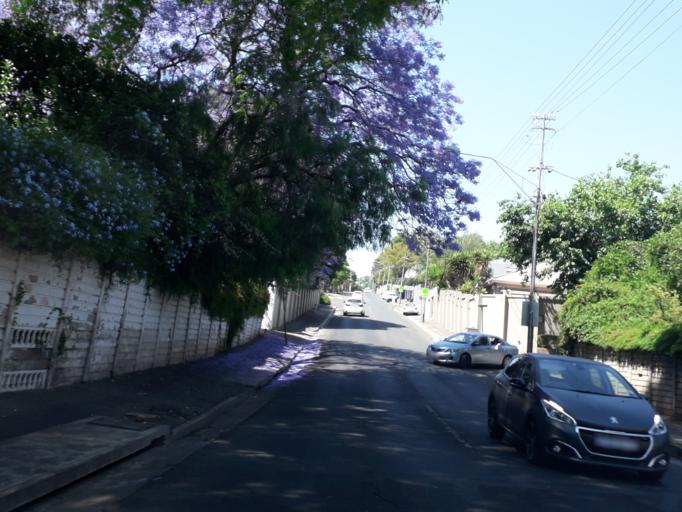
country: ZA
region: Gauteng
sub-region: City of Johannesburg Metropolitan Municipality
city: Johannesburg
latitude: -26.1389
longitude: 28.0238
